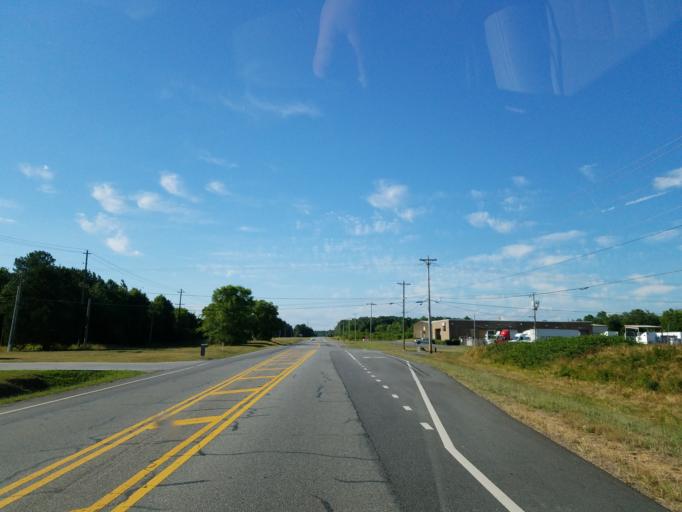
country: US
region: Georgia
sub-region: Gordon County
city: Calhoun
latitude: 34.4610
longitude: -84.9344
